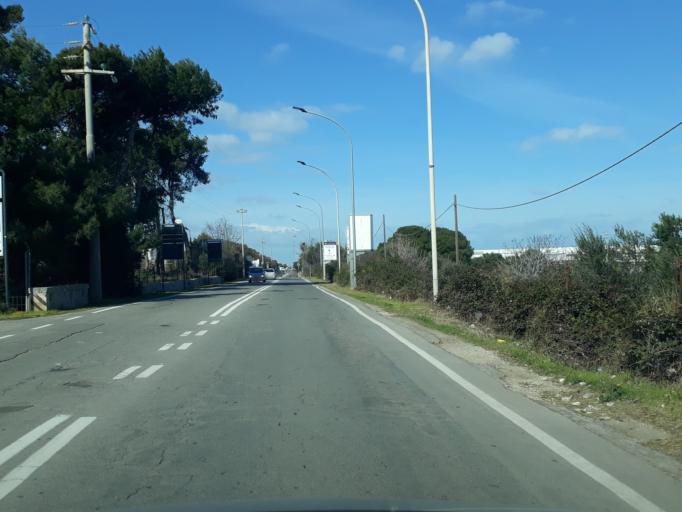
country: IT
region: Apulia
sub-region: Provincia di Bari
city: Monopoli
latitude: 40.9627
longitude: 17.2795
